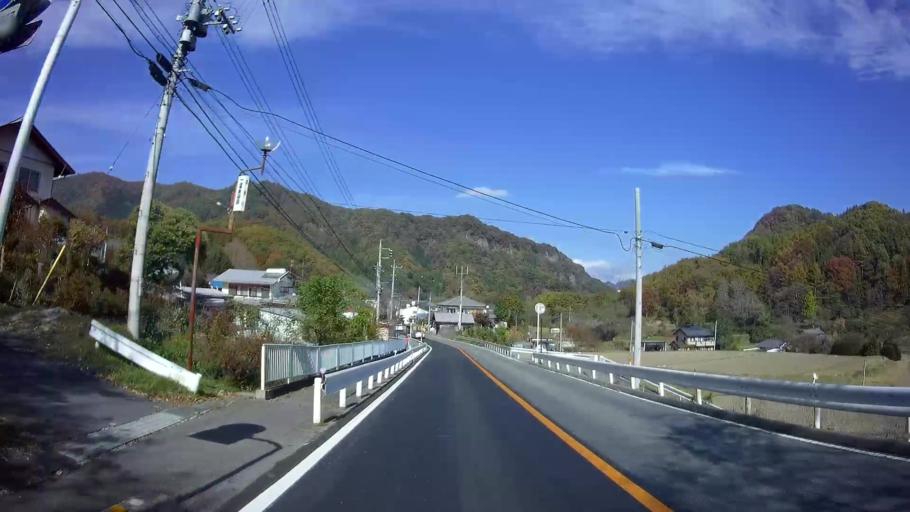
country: JP
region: Gunma
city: Nakanojomachi
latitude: 36.5091
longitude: 138.7755
